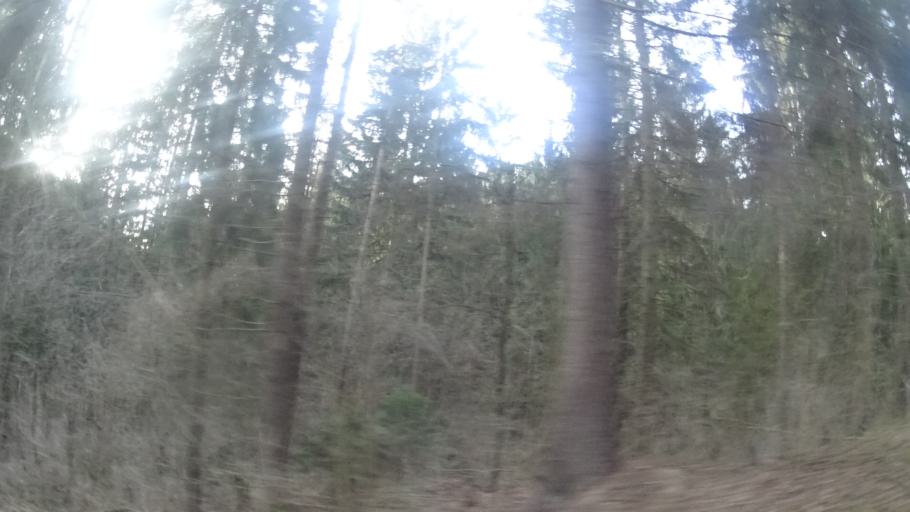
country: DE
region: Thuringia
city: Rottenbach
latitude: 50.7294
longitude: 11.1983
